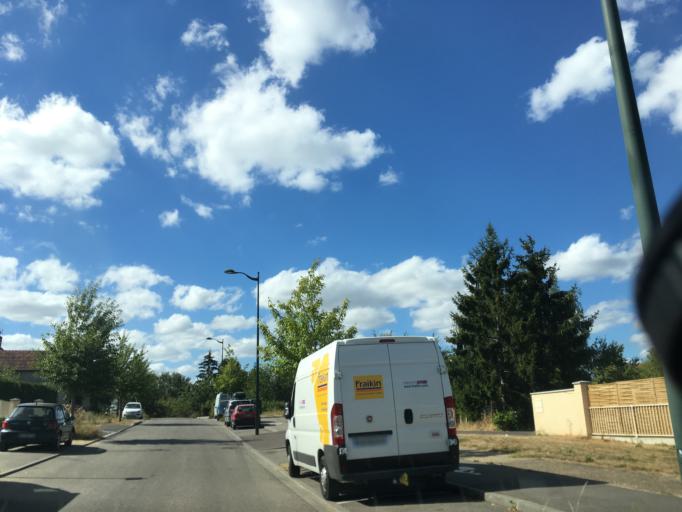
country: FR
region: Haute-Normandie
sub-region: Departement de l'Eure
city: Vernon
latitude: 49.0811
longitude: 1.4957
